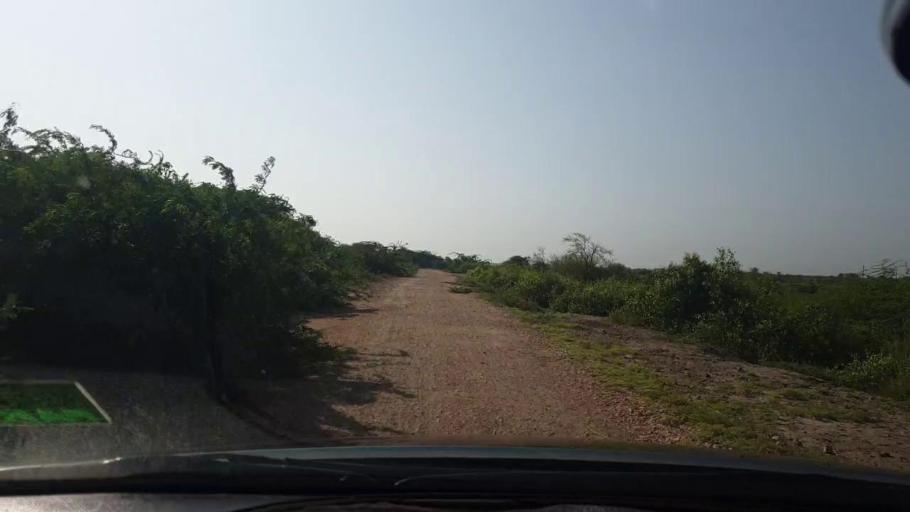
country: PK
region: Sindh
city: Tando Bago
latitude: 24.7140
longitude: 68.9780
